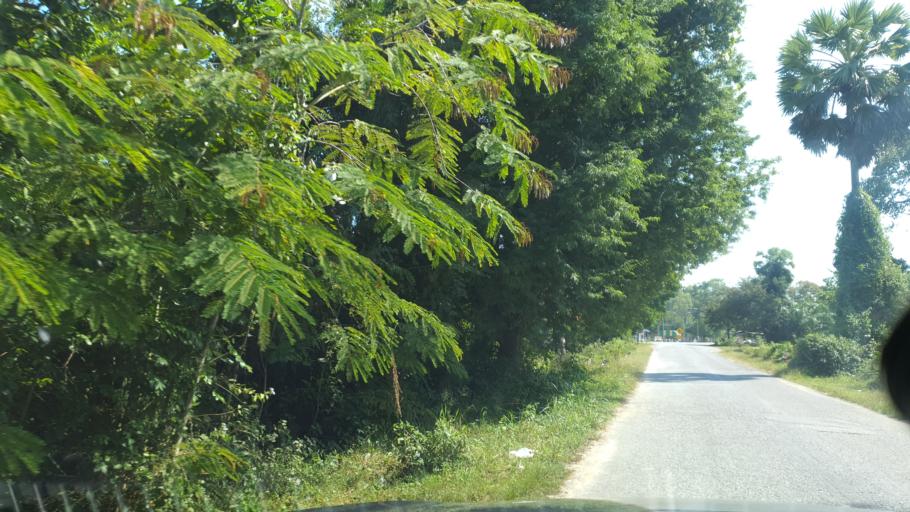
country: TH
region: Surat Thani
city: Tha Chana
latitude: 9.5882
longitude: 99.2014
